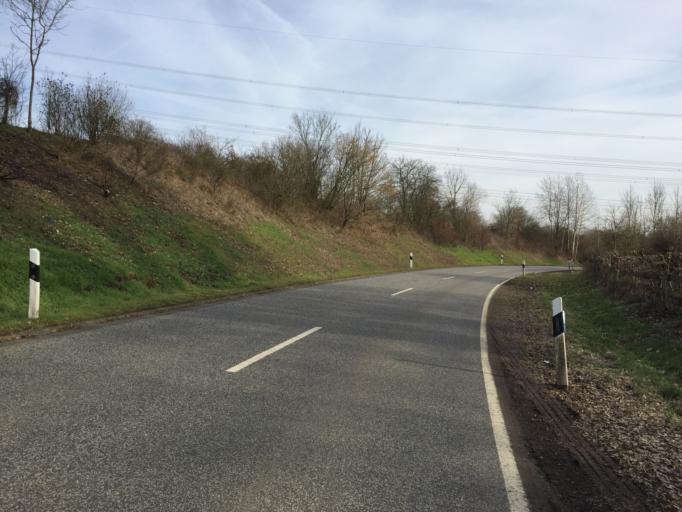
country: DE
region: Hesse
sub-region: Regierungsbezirk Giessen
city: Fronhausen
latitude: 50.6806
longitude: 8.6922
